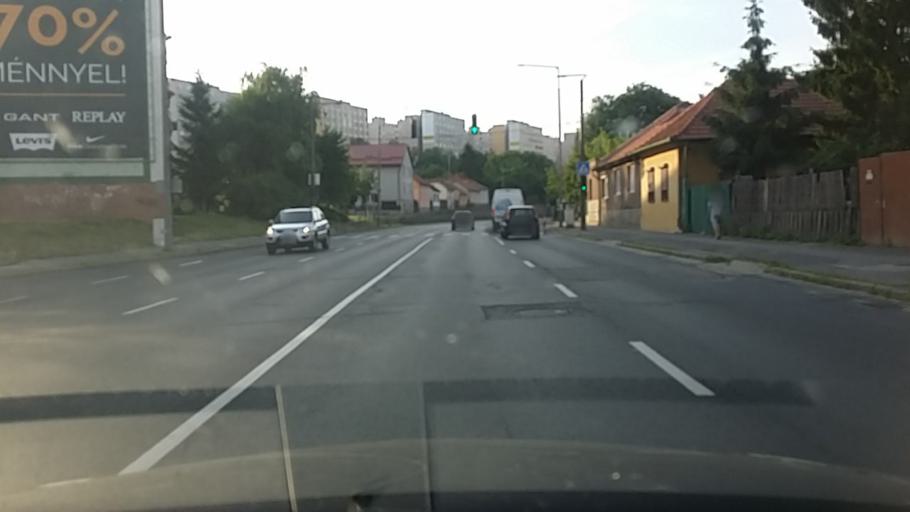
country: HU
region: Borsod-Abauj-Zemplen
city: Miskolc
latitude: 48.0758
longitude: 20.7856
